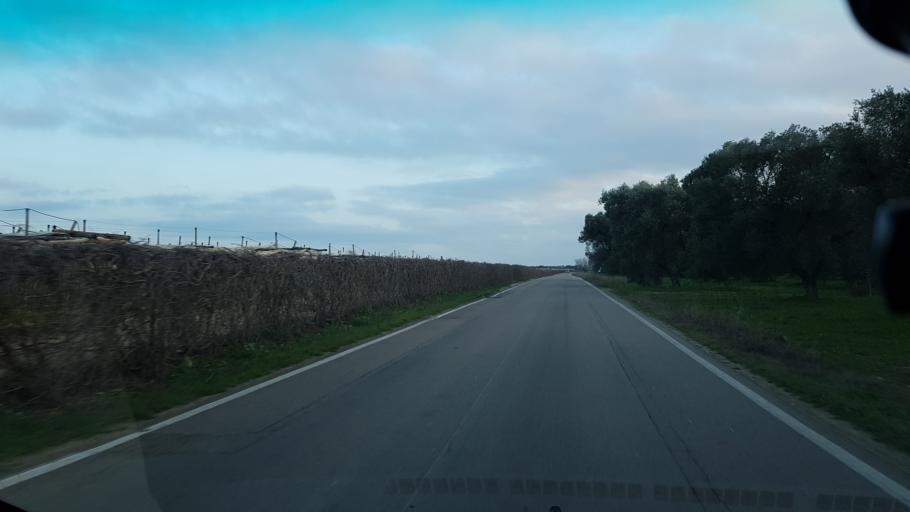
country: IT
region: Apulia
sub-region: Provincia di Brindisi
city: Mesagne
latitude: 40.6312
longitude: 17.7826
